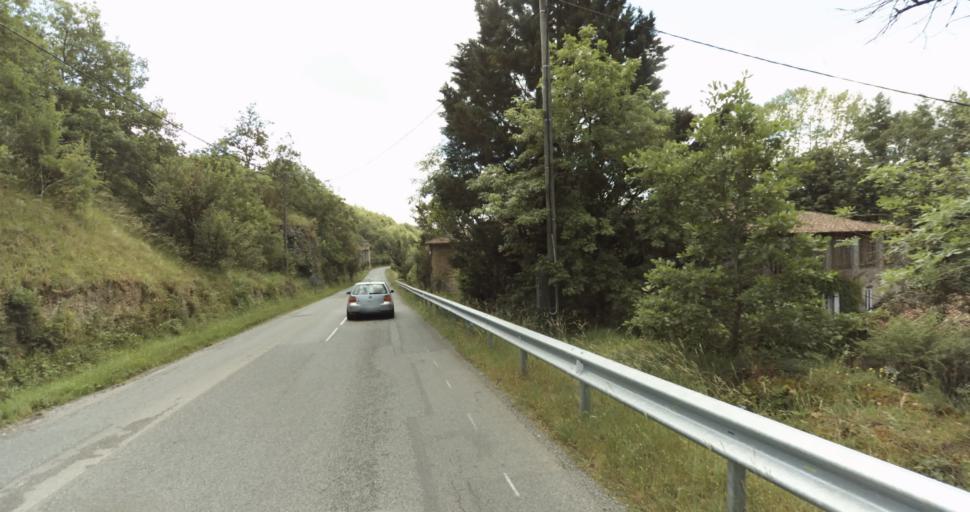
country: FR
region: Aquitaine
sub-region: Departement de la Dordogne
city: Lalinde
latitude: 44.8188
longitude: 0.7088
